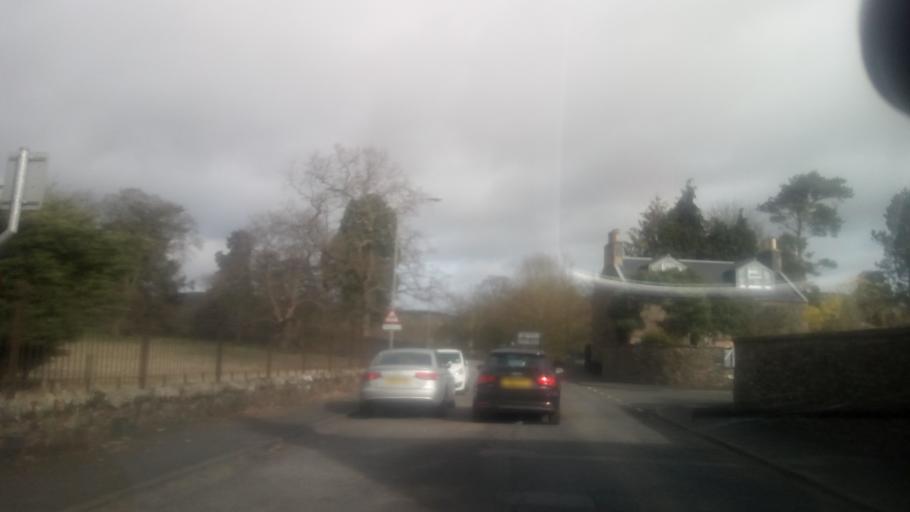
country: GB
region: Scotland
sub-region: The Scottish Borders
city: Melrose
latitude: 55.6013
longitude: -2.7448
